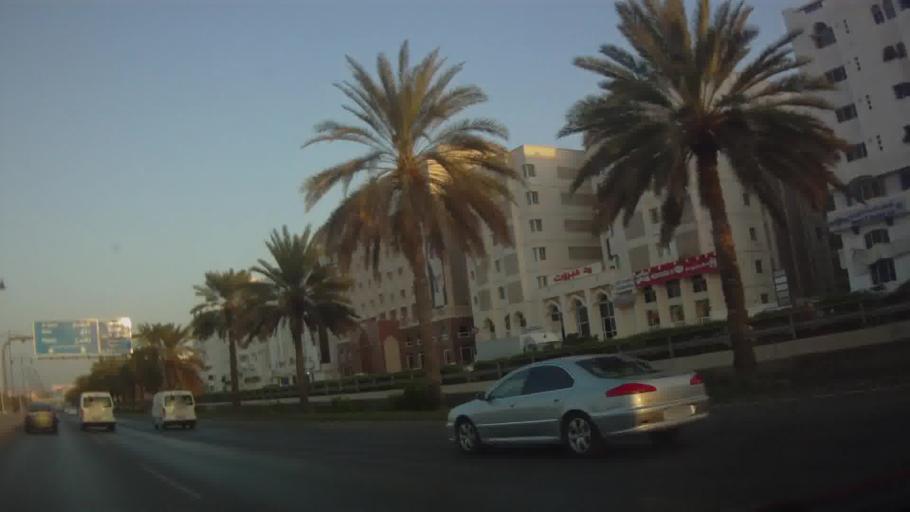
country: OM
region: Muhafazat Masqat
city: Bawshar
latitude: 23.5971
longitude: 58.4290
